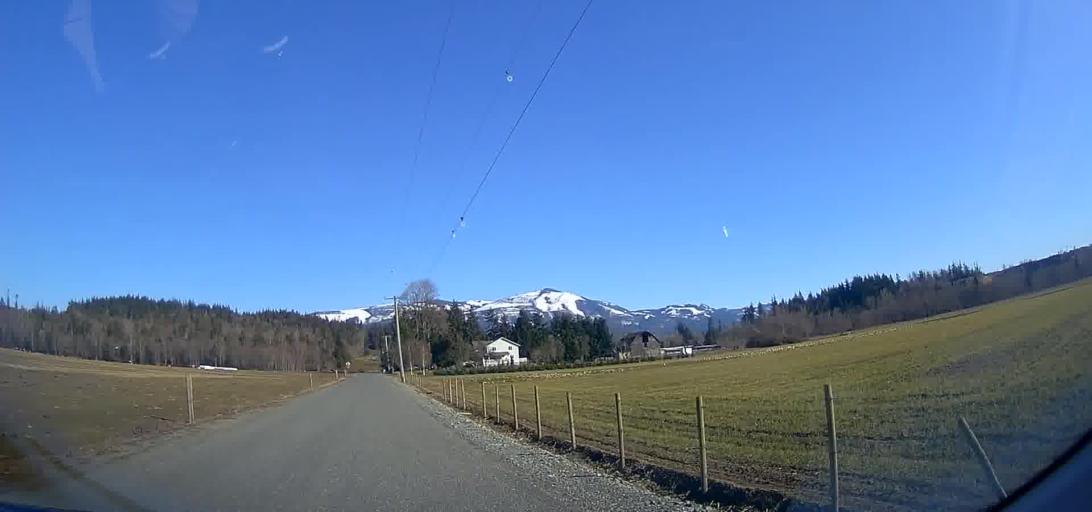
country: US
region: Washington
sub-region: Skagit County
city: Clear Lake
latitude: 48.4494
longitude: -122.2630
